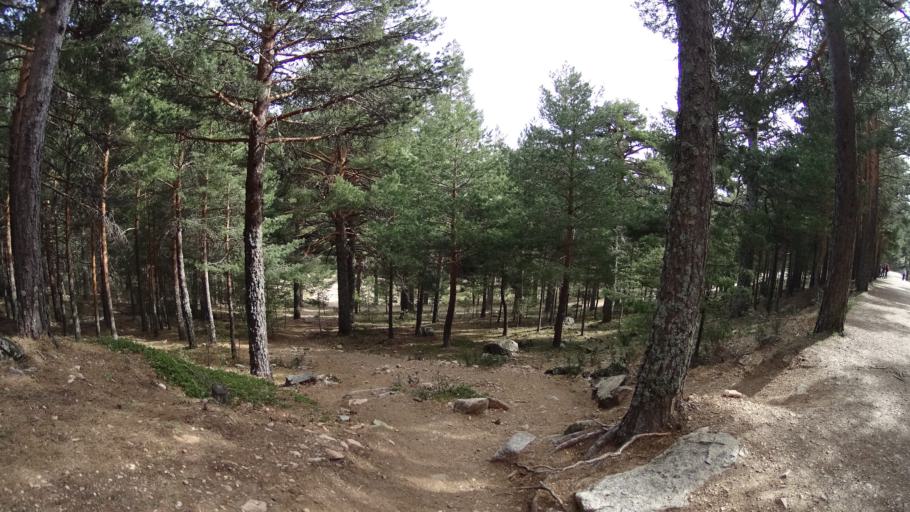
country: ES
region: Madrid
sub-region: Provincia de Madrid
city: Navacerrada
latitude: 40.7627
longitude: -3.9962
